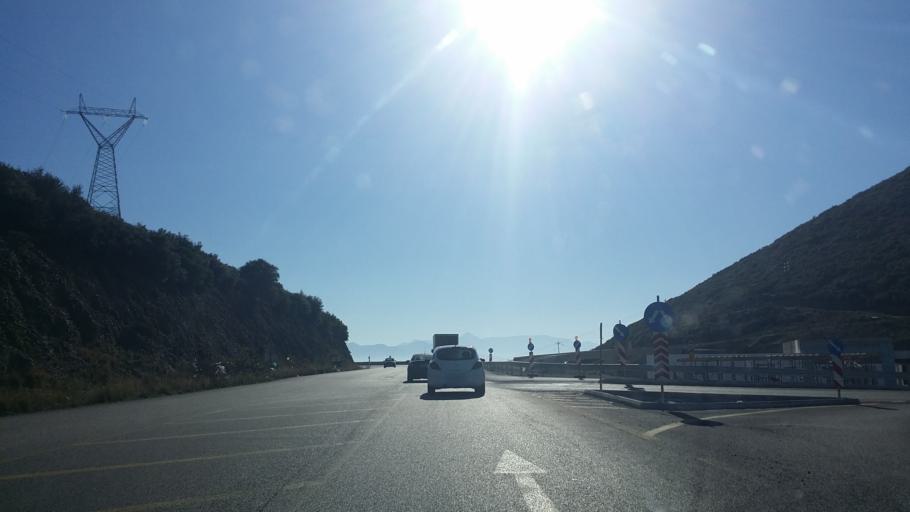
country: GR
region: West Greece
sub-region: Nomos Aitolias kai Akarnanias
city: Galatas
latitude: 38.3593
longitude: 21.6592
